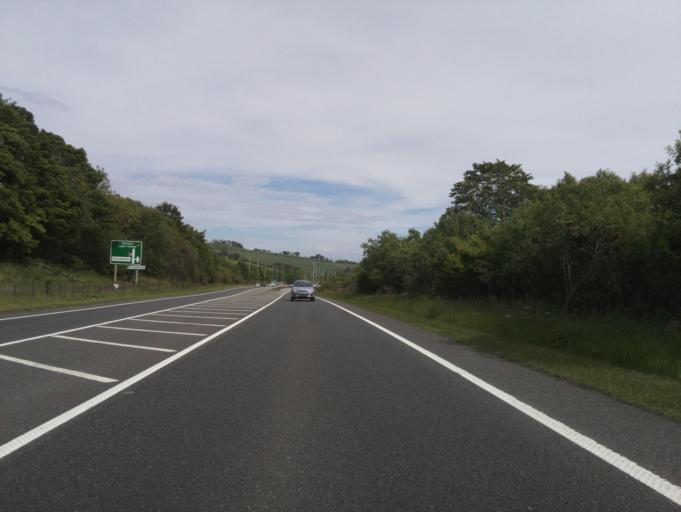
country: GB
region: Scotland
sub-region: The Scottish Borders
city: Chirnside
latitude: 55.8684
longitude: -2.2640
